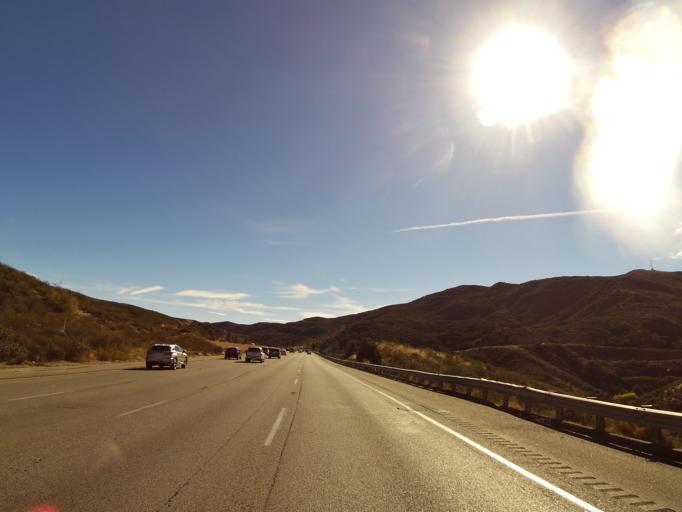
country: US
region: California
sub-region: Los Angeles County
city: Castaic
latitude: 34.5959
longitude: -118.7122
